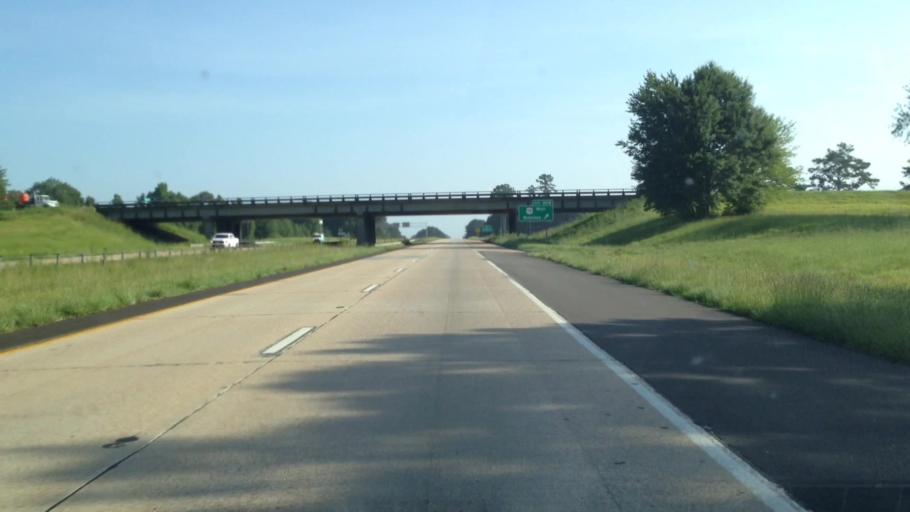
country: US
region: Mississippi
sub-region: Pike County
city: Summit
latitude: 31.2873
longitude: -90.4785
